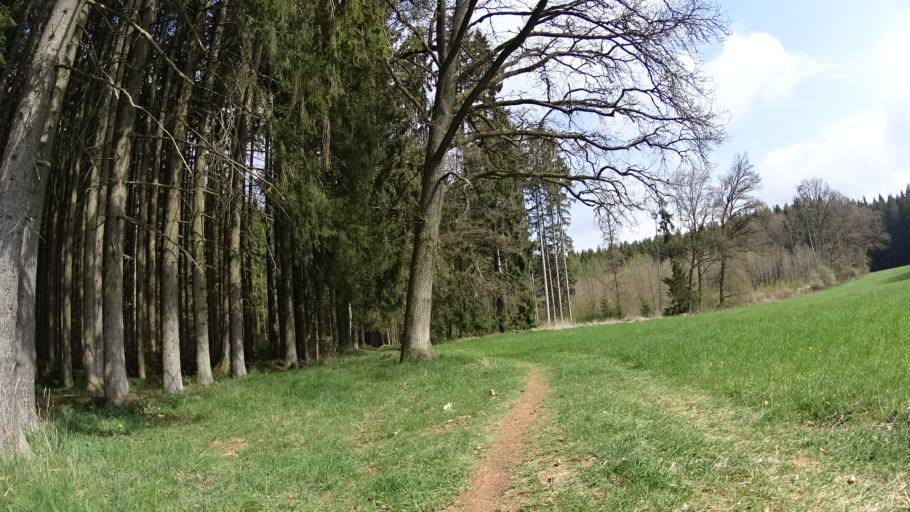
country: DE
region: Bavaria
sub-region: Upper Bavaria
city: Bohmfeld
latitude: 48.8607
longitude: 11.4034
